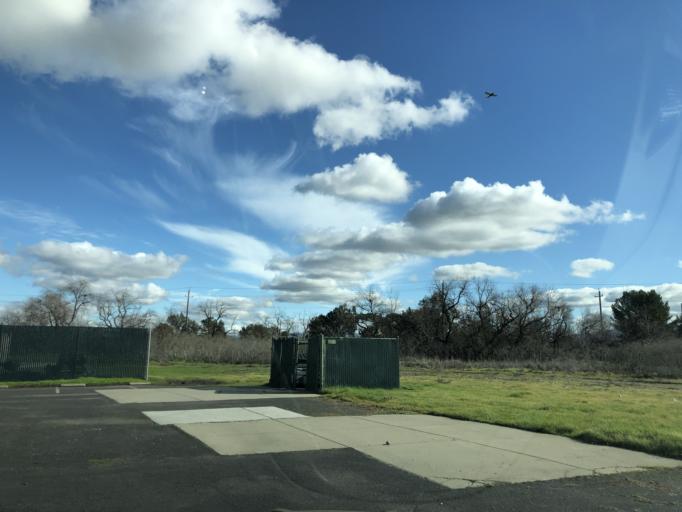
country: US
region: California
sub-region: Alameda County
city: Pleasanton
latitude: 37.6973
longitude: -121.8368
